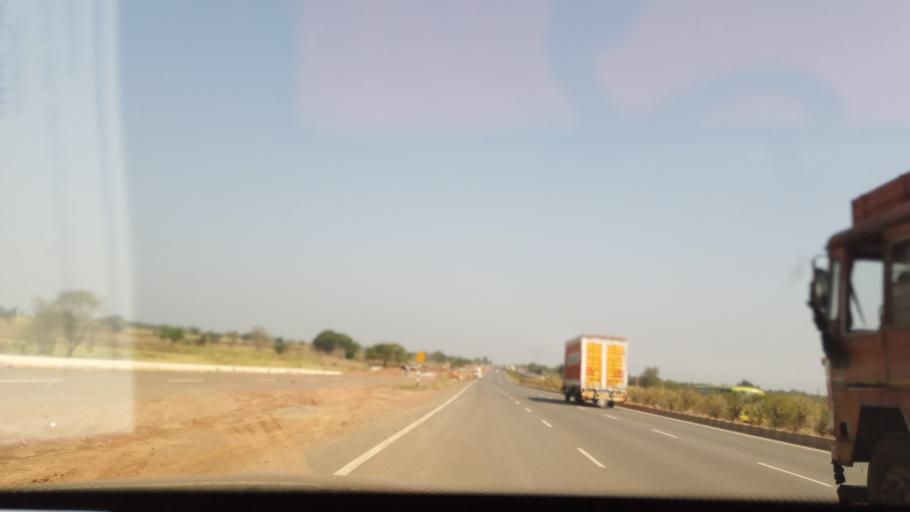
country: IN
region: Karnataka
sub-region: Dharwad
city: Kundgol
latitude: 15.1384
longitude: 75.1462
